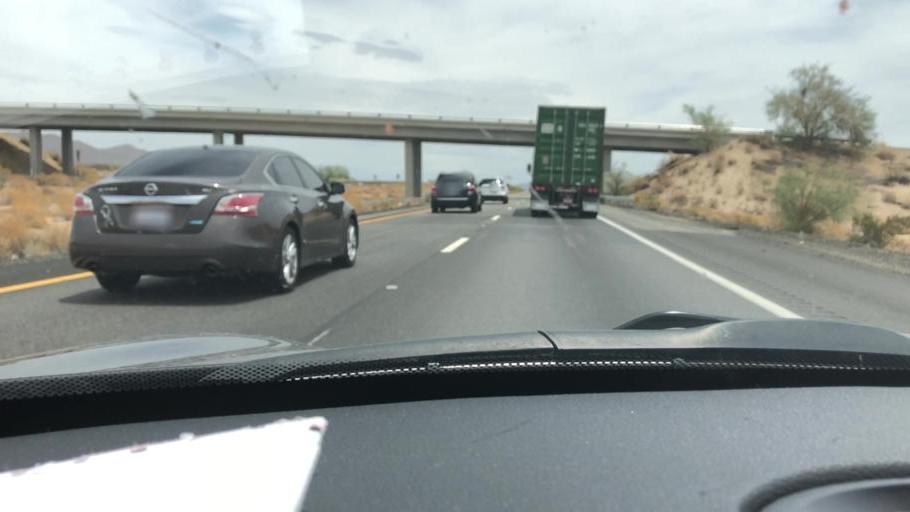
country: US
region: California
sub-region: Riverside County
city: Mecca
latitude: 33.6600
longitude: -115.8032
